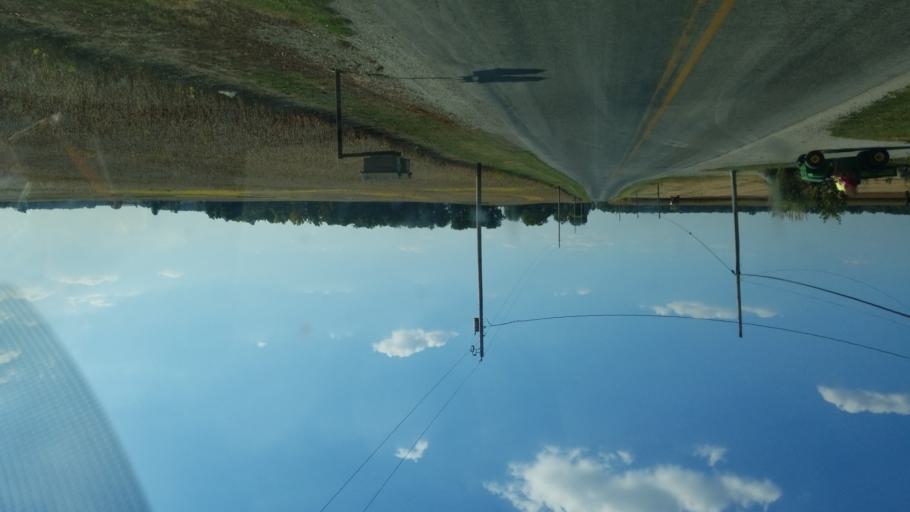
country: US
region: Ohio
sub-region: Union County
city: Richwood
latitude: 40.5578
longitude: -83.3915
